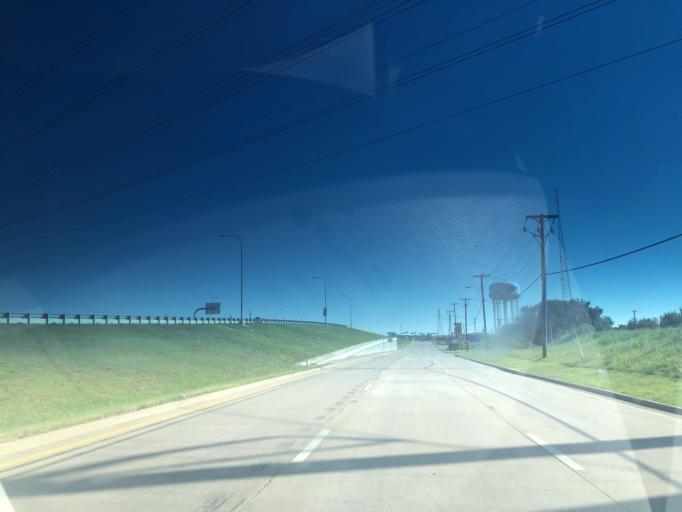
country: US
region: Texas
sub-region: Dallas County
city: Grand Prairie
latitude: 32.7189
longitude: -97.0230
